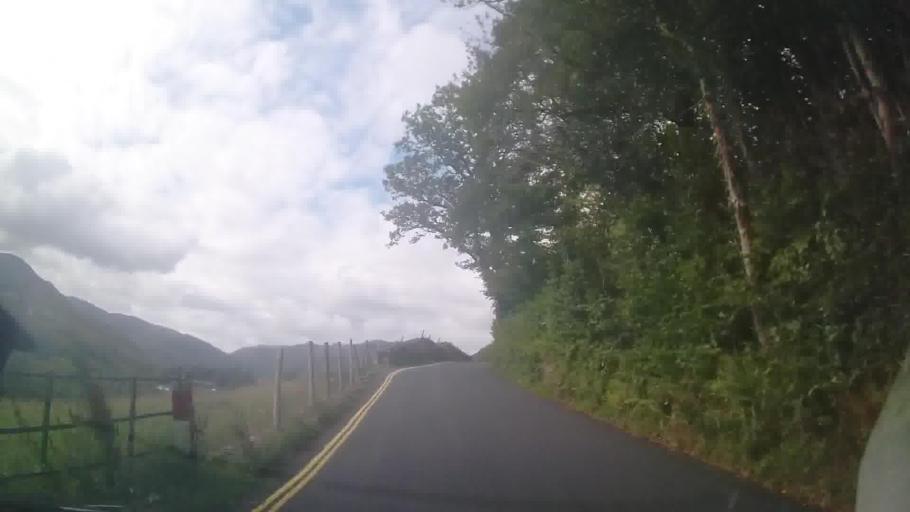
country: GB
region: England
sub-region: Cumbria
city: Ambleside
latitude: 54.4190
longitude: -3.0481
